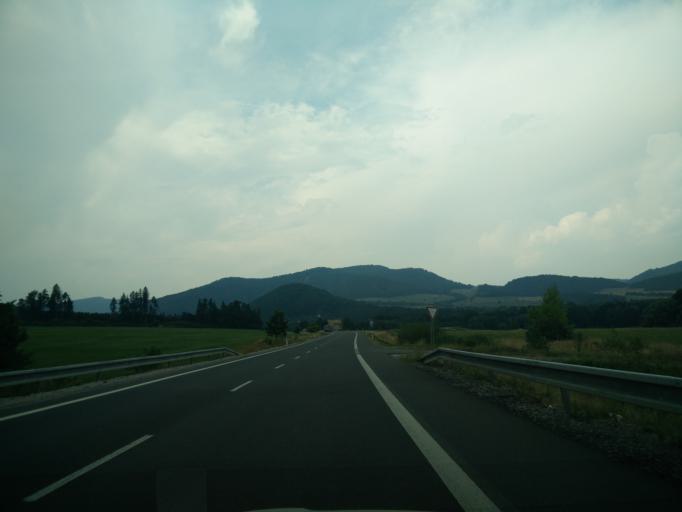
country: SK
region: Nitriansky
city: Handlova
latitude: 48.6408
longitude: 18.7714
